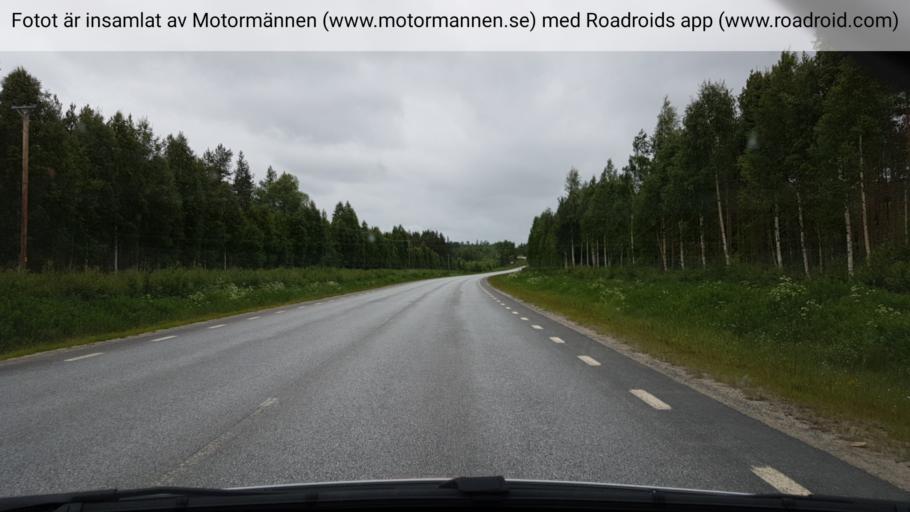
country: SE
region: Vaesterbotten
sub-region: Vannas Kommun
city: Vaennaes
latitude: 64.0219
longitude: 19.6920
